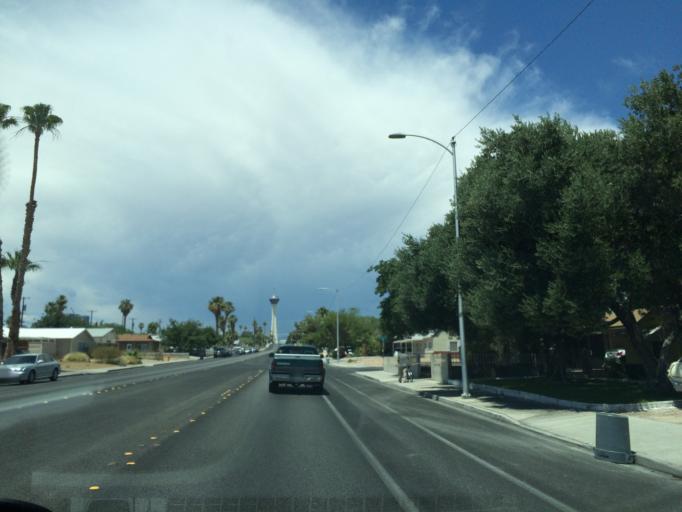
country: US
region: Nevada
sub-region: Clark County
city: Winchester
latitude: 36.1482
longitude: -115.1245
